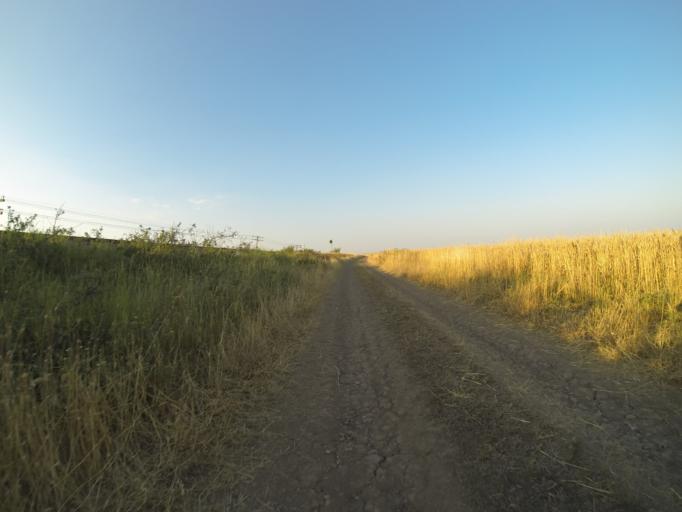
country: RO
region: Dolj
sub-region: Comuna Ceratu
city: Ceratu
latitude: 44.0695
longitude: 23.7031
